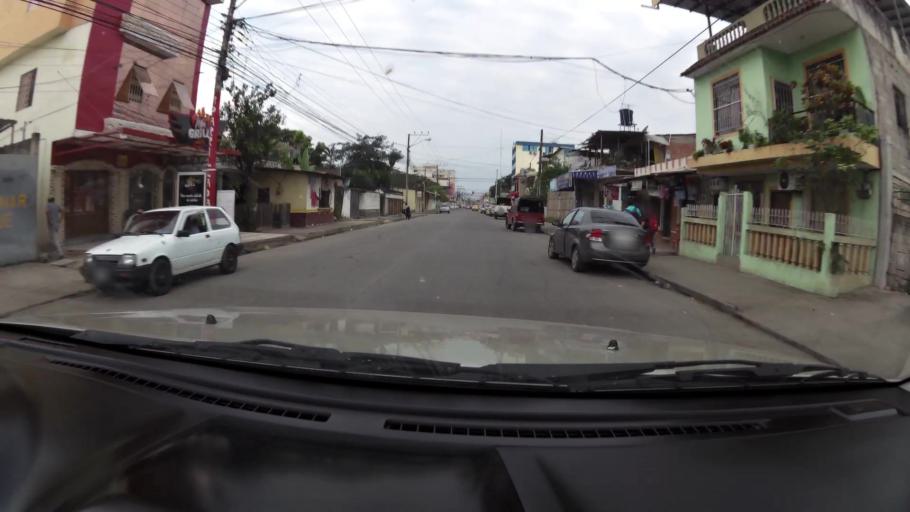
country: EC
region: El Oro
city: Machala
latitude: -3.2611
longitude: -79.9479
